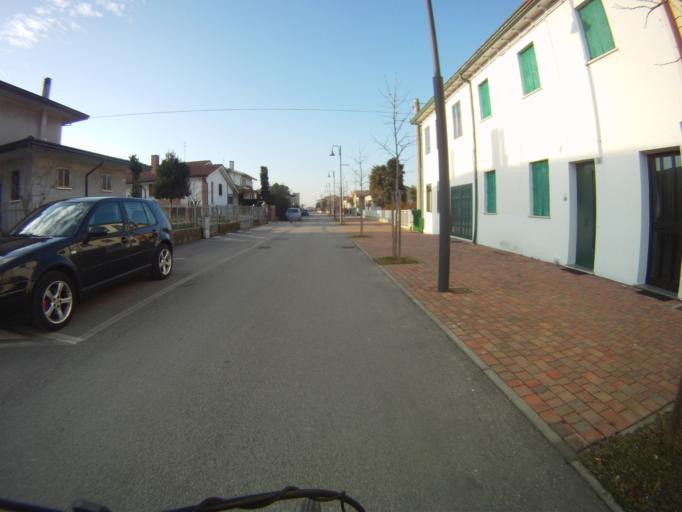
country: IT
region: Veneto
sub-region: Provincia di Padova
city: Polverara
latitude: 45.3105
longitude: 11.9566
